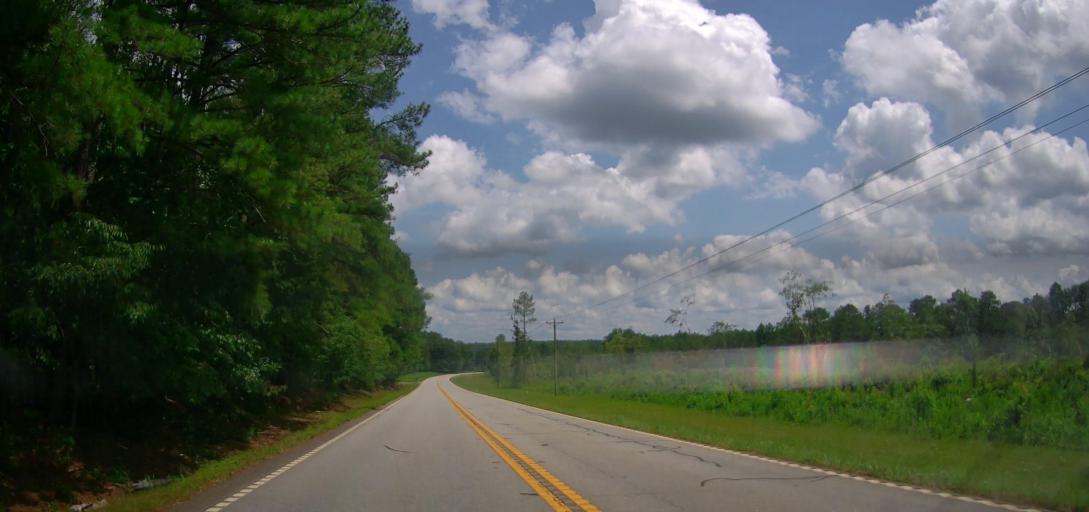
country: US
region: Georgia
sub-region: Heard County
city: Franklin
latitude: 33.3359
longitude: -85.1643
